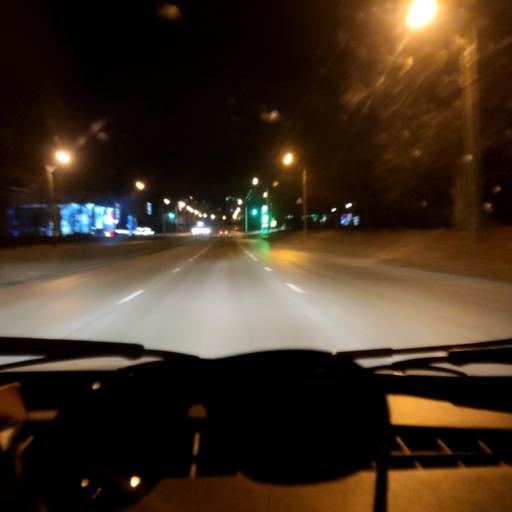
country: RU
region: Bashkortostan
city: Ufa
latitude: 54.7328
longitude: 56.0256
